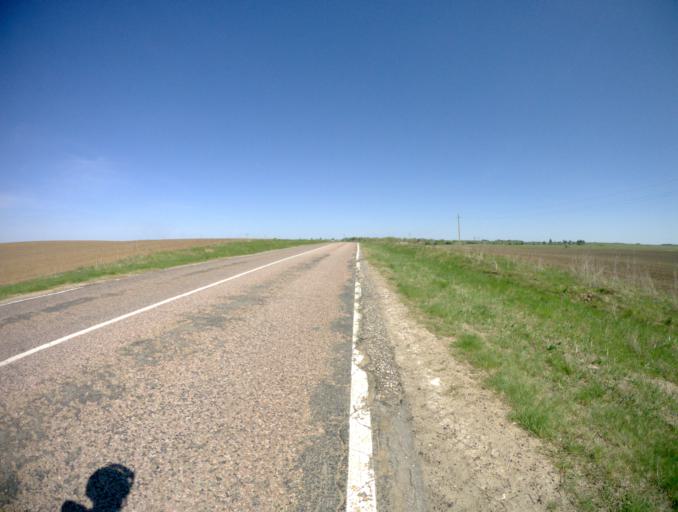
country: RU
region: Vladimir
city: Suzdal'
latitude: 56.3697
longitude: 40.4129
